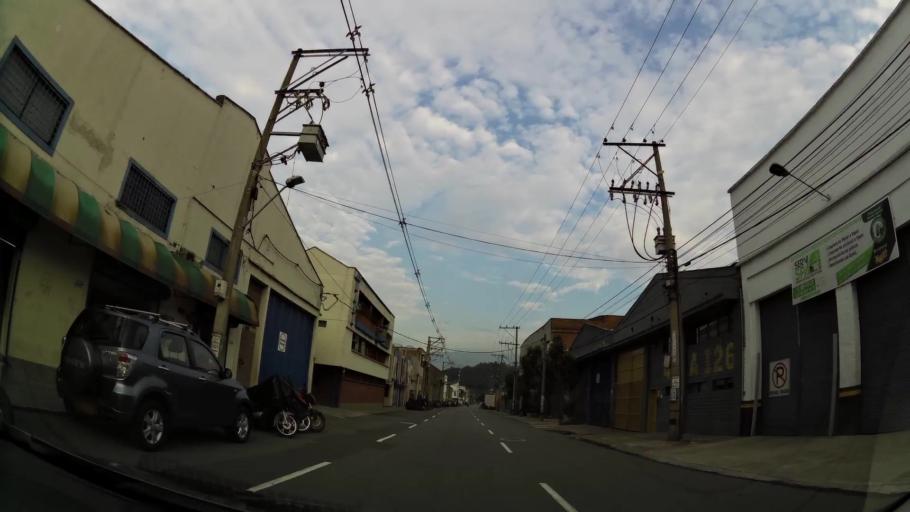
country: CO
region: Antioquia
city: Medellin
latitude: 6.2316
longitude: -75.5710
